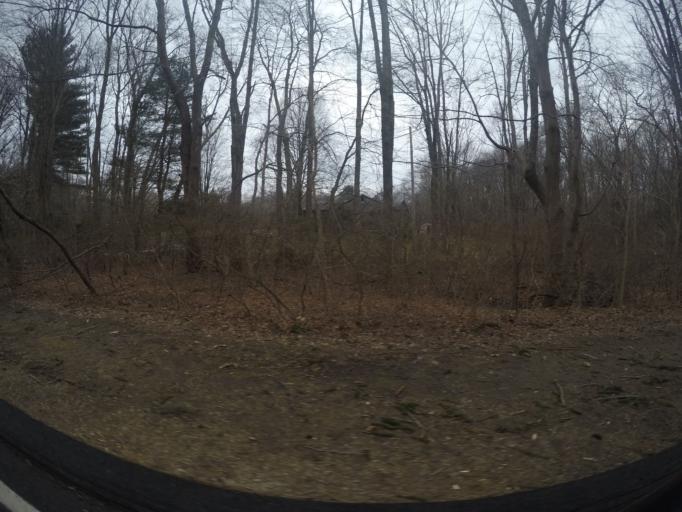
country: US
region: Massachusetts
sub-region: Bristol County
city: Easton
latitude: 42.0445
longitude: -71.1521
